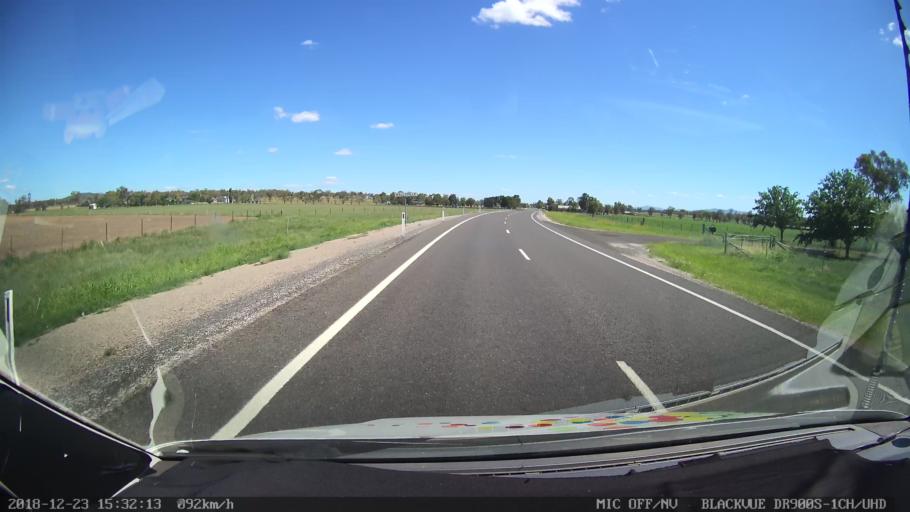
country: AU
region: New South Wales
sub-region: Tamworth Municipality
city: East Tamworth
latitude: -30.9825
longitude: 150.8701
